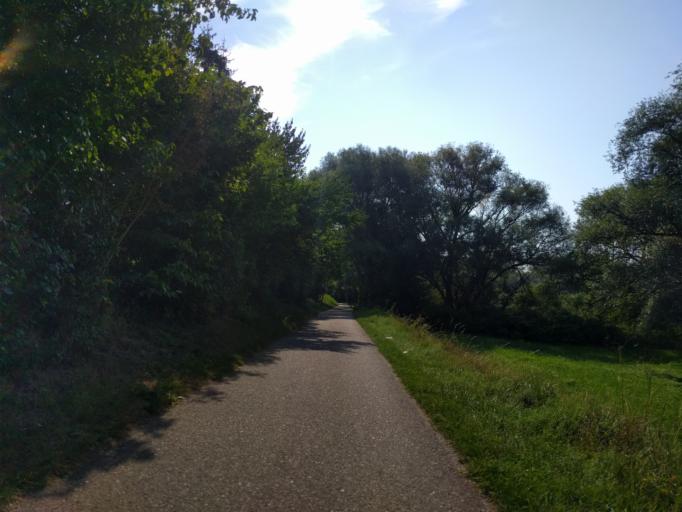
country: DE
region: Bavaria
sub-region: Upper Palatinate
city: Tegernheim
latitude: 49.0206
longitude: 12.1541
